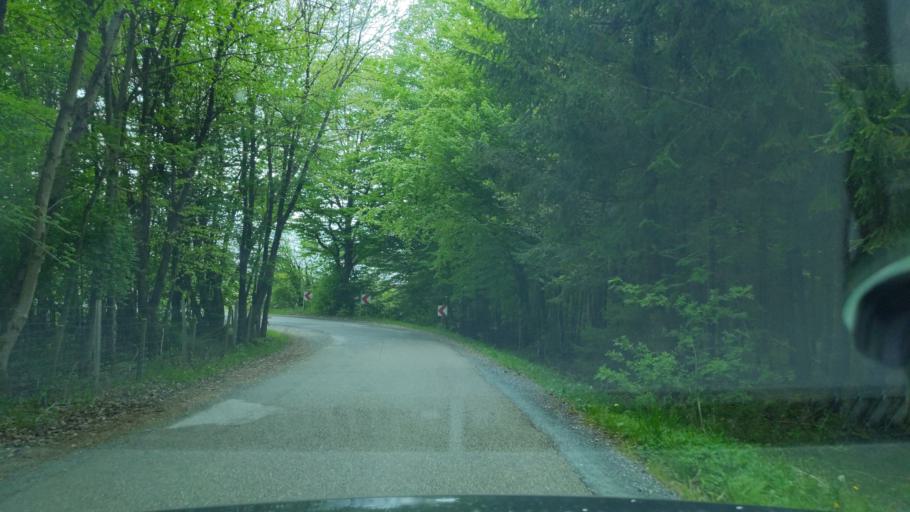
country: DE
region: Bavaria
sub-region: Upper Bavaria
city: Ebersberg
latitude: 48.1125
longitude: 11.9835
